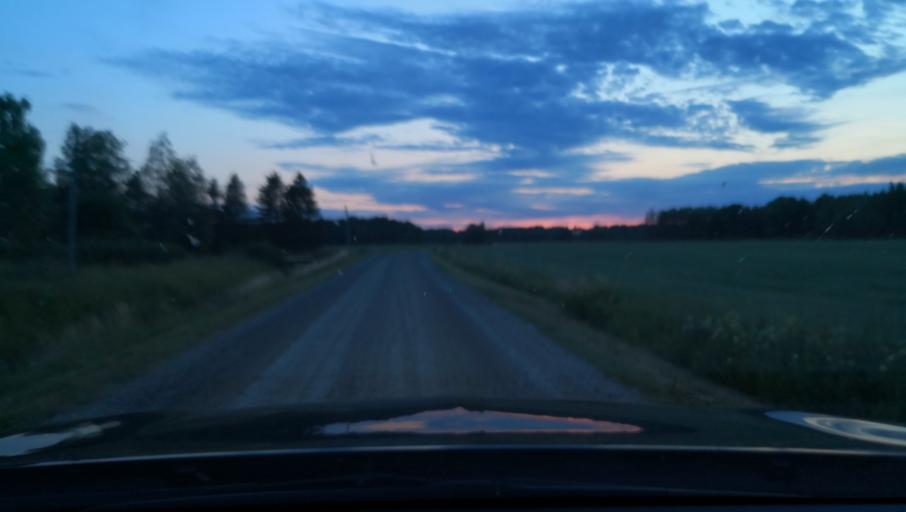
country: SE
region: Uppsala
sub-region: Heby Kommun
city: OEstervala
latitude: 60.0126
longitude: 17.3130
